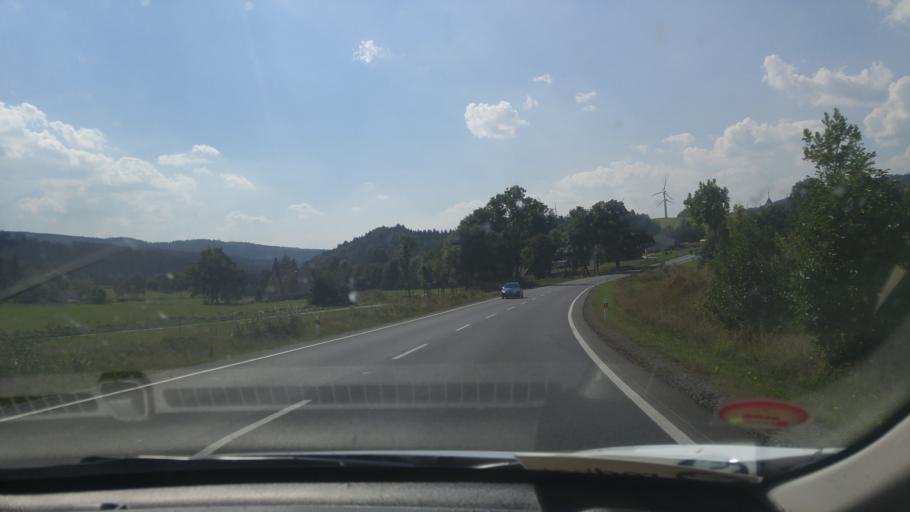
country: CZ
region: Olomoucky
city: Vapenna
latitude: 50.1877
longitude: 17.0576
